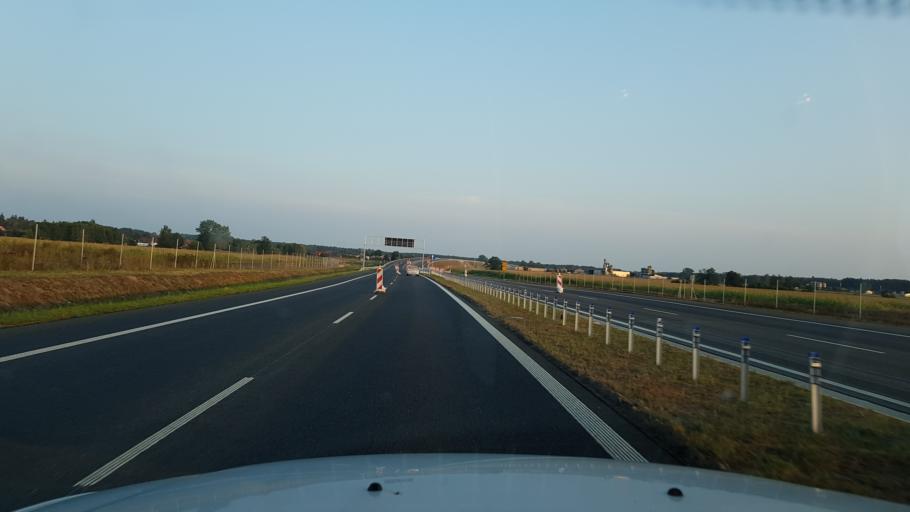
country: PL
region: West Pomeranian Voivodeship
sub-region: Powiat gryficki
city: Ploty
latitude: 53.8055
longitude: 15.2488
